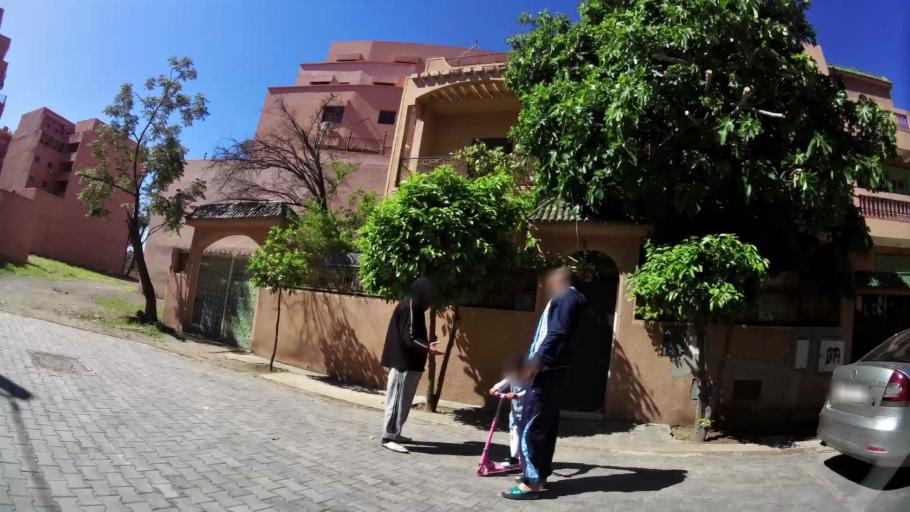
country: MA
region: Marrakech-Tensift-Al Haouz
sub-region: Marrakech
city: Marrakesh
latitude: 31.6431
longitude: -8.0107
